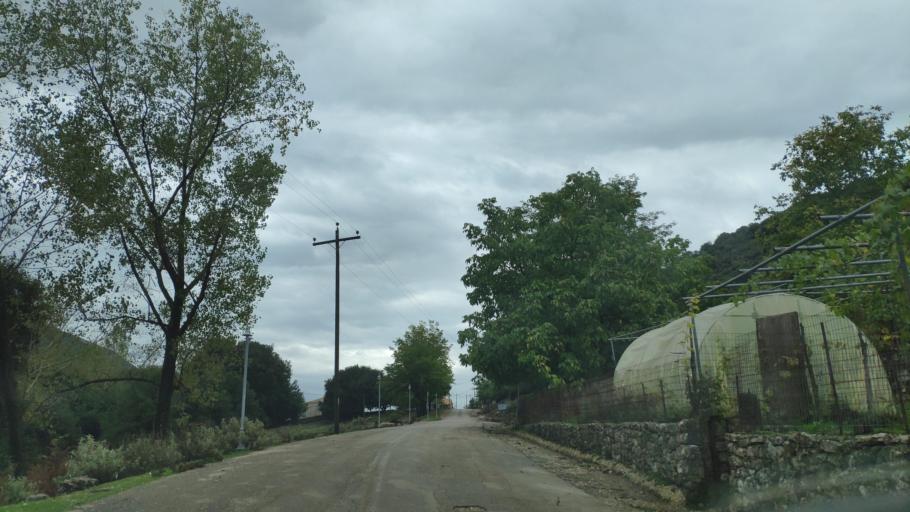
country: GR
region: Epirus
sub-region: Nomos Prevezis
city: Kanalaki
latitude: 39.3614
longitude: 20.6406
